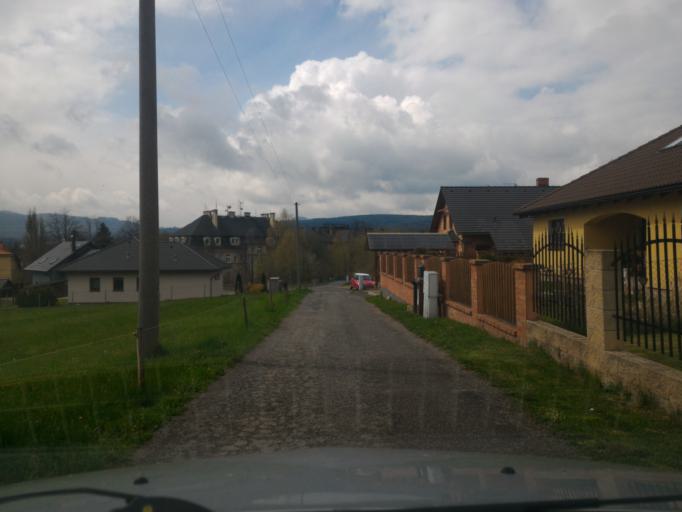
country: CZ
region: Ustecky
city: Varnsdorf
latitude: 50.9202
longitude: 14.6203
